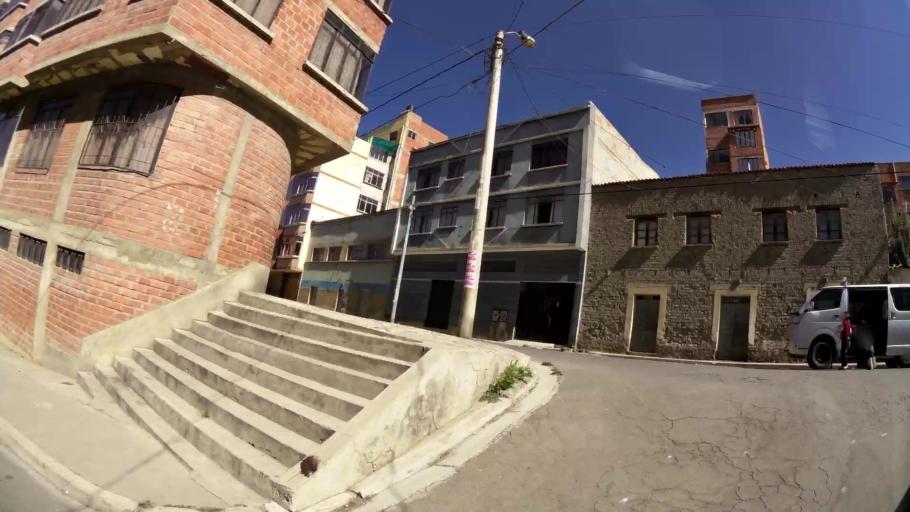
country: BO
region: La Paz
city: La Paz
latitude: -16.4919
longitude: -68.1600
